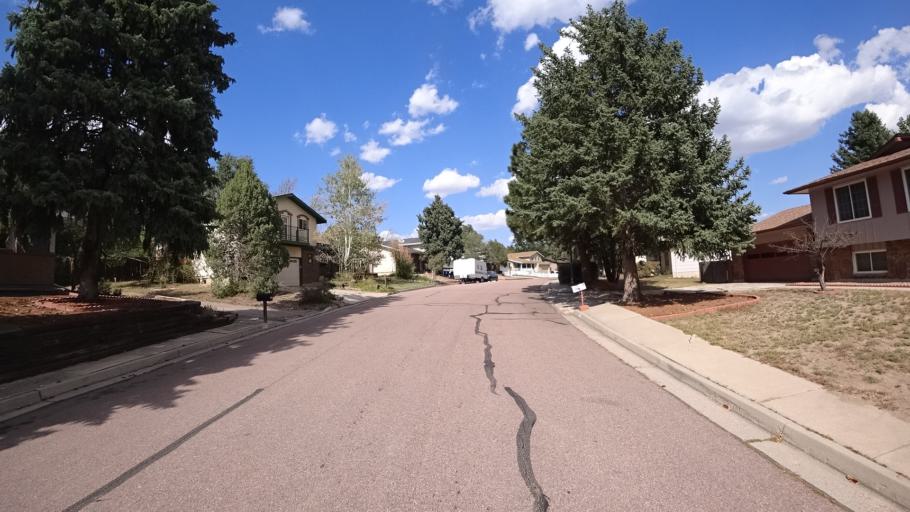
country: US
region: Colorado
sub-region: El Paso County
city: Cimarron Hills
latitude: 38.8700
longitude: -104.7342
